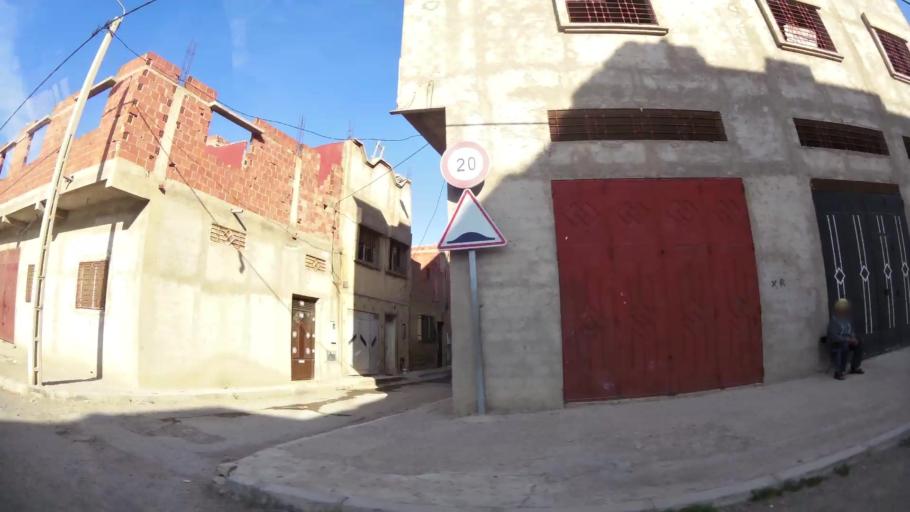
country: MA
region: Oriental
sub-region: Oujda-Angad
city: Oujda
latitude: 34.7121
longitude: -1.8944
